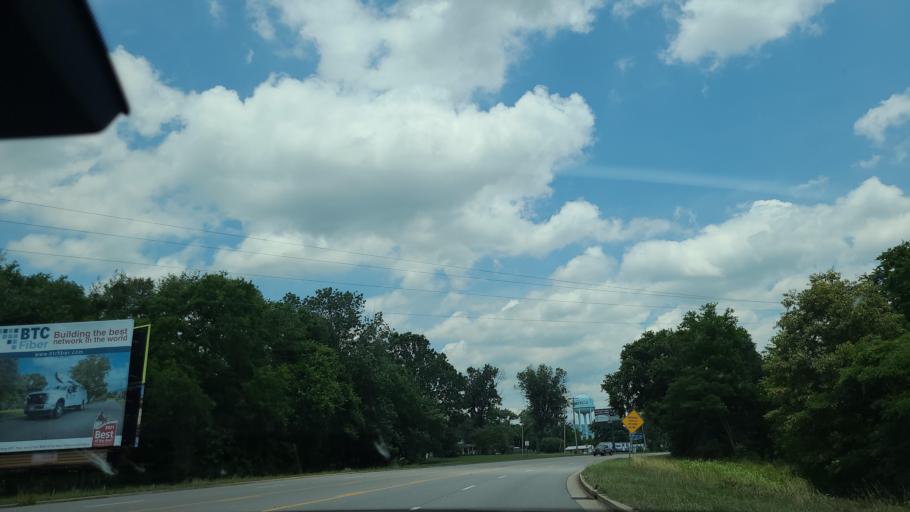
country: US
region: Tennessee
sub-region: Bledsoe County
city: Pikeville
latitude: 35.6060
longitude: -85.1976
